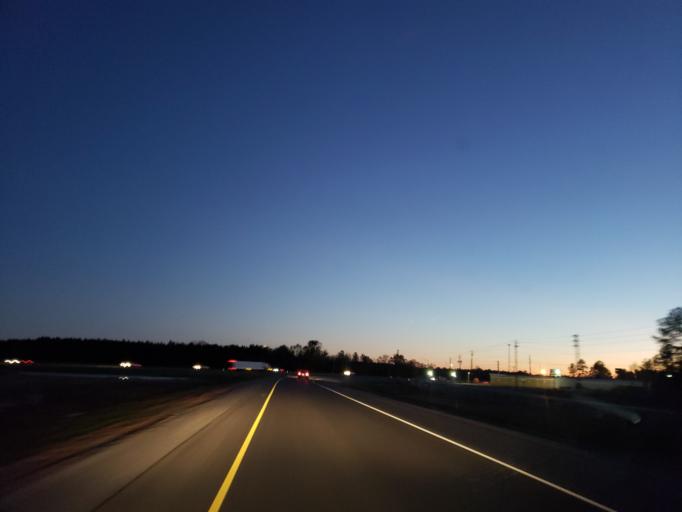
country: US
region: Mississippi
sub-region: Forrest County
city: Glendale
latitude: 31.3806
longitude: -89.3272
